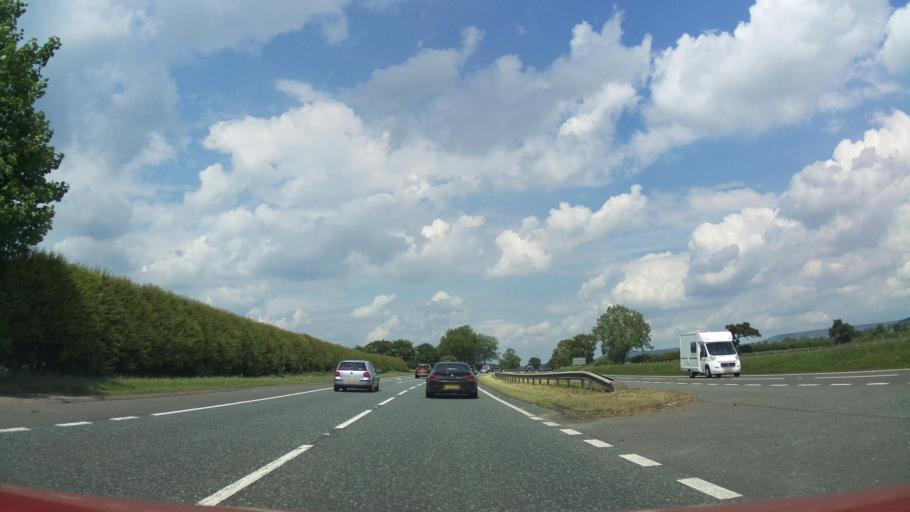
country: GB
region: England
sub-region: North Yorkshire
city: Thirsk
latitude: 54.2608
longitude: -1.3489
